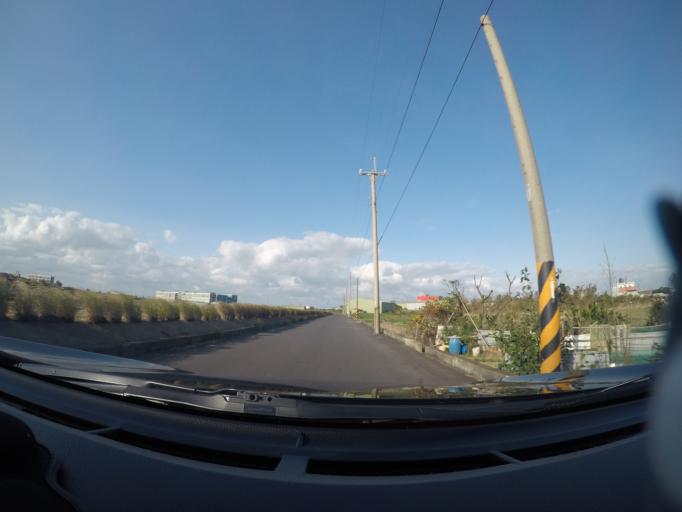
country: TW
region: Taiwan
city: Taoyuan City
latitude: 25.1023
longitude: 121.2520
